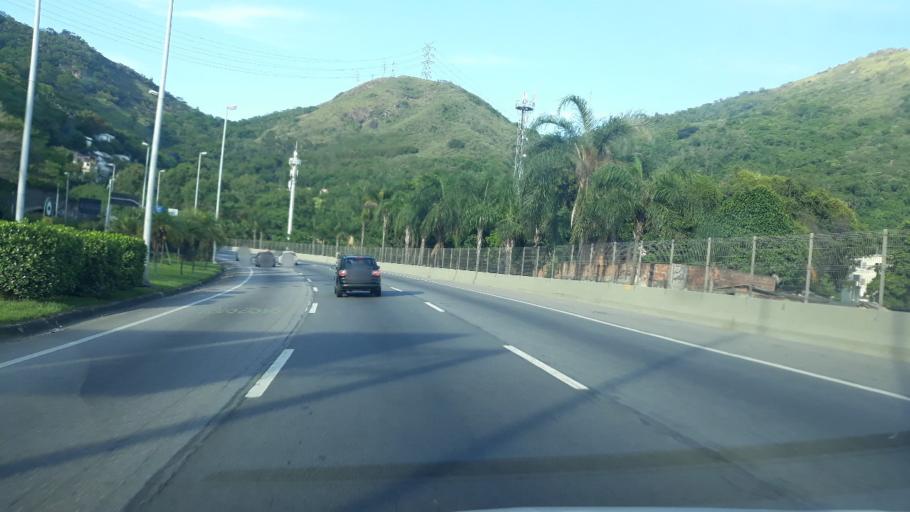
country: BR
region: Rio de Janeiro
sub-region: Rio De Janeiro
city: Rio de Janeiro
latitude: -22.9070
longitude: -43.3132
